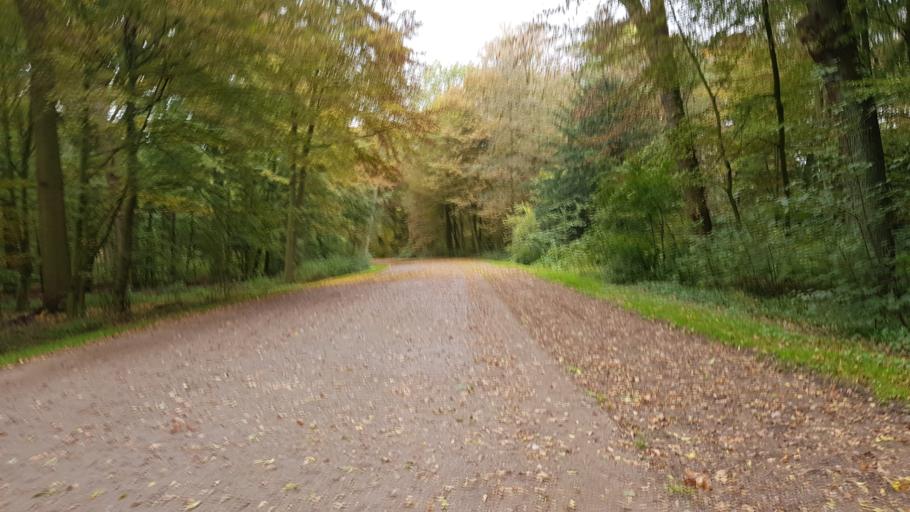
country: DE
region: Bremen
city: Bremen
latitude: 53.0958
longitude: 8.8241
